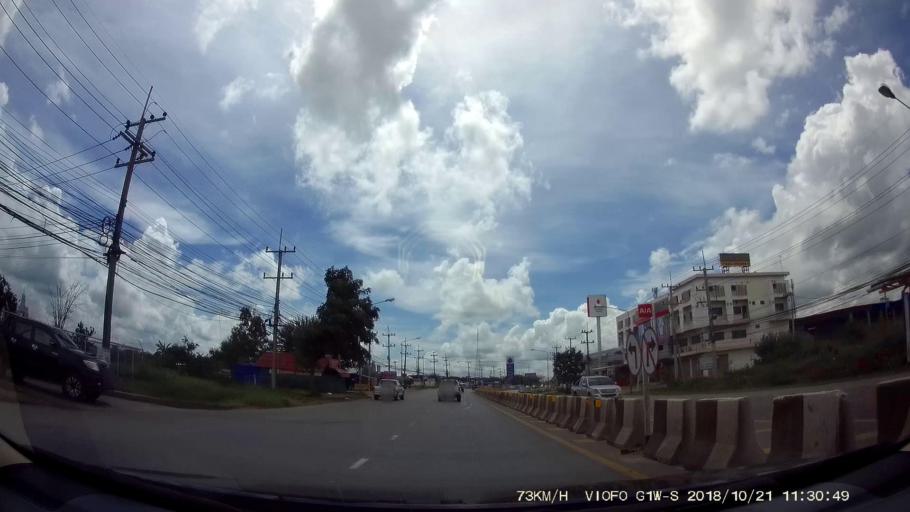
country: TH
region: Chaiyaphum
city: Chaiyaphum
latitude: 15.7746
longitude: 102.0260
